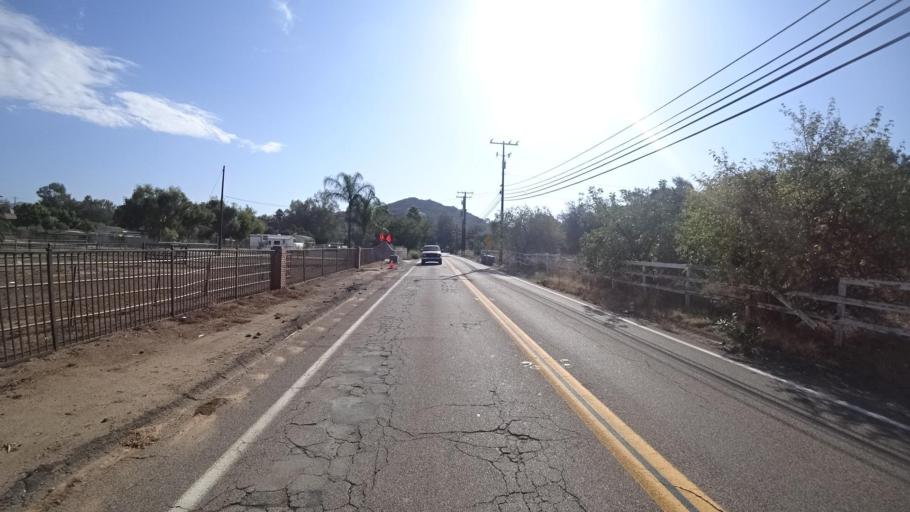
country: US
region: California
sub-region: San Diego County
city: Valley Center
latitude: 33.2019
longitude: -116.9687
